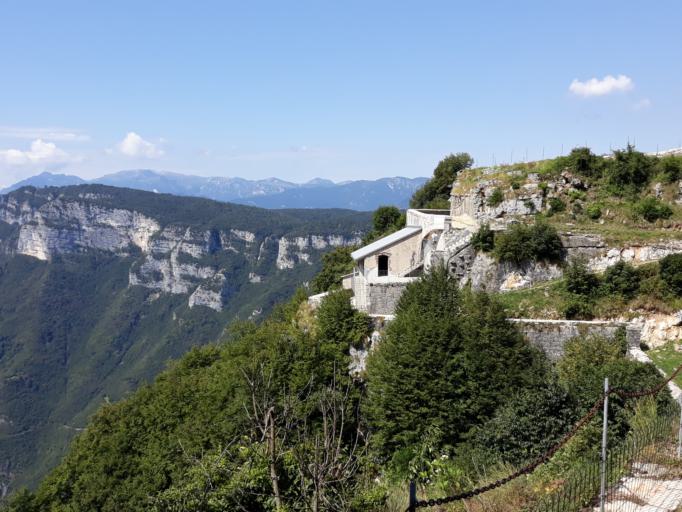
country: IT
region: Veneto
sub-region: Provincia di Vicenza
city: Rotzo
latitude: 45.8333
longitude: 11.3870
